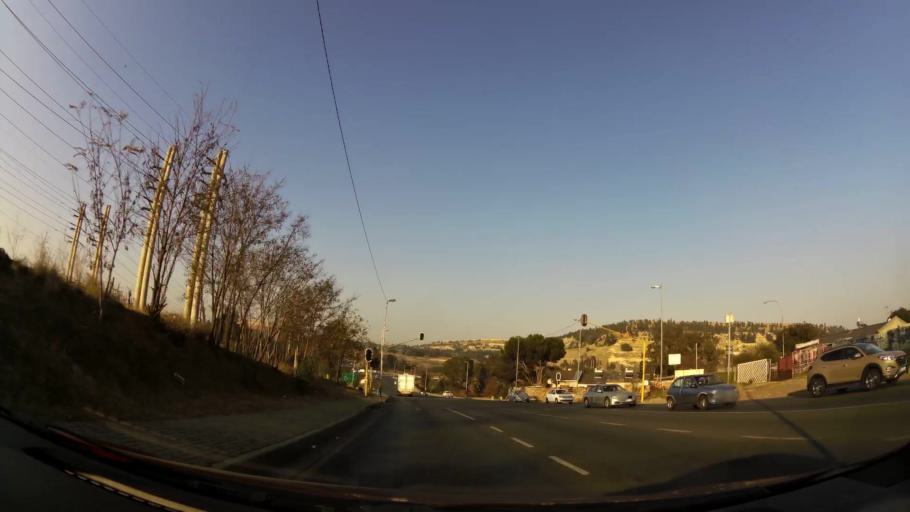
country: ZA
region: Gauteng
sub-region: City of Johannesburg Metropolitan Municipality
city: Johannesburg
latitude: -26.2188
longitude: 27.9813
